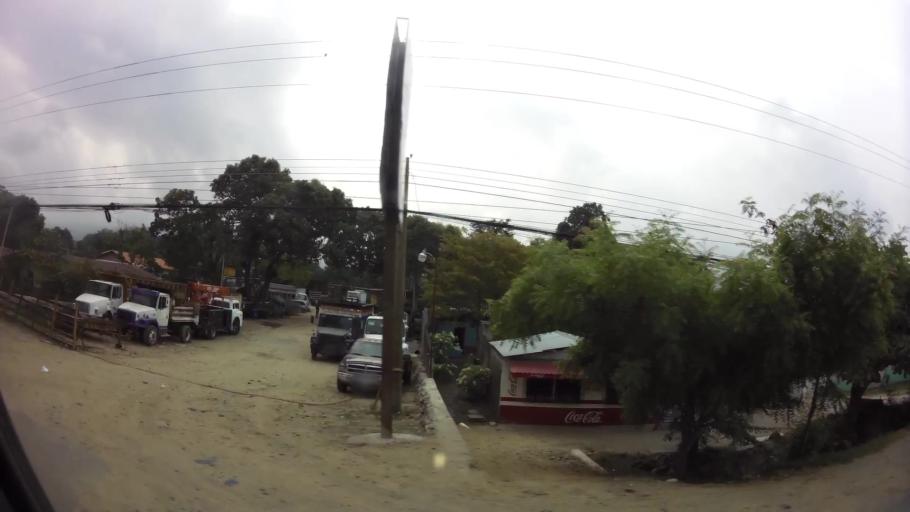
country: HN
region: Yoro
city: El Progreso
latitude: 15.4269
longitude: -87.7977
